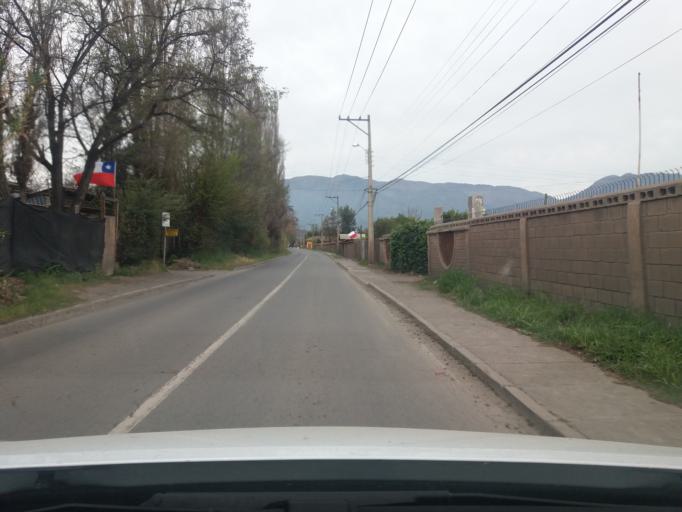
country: CL
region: Valparaiso
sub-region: Provincia de Los Andes
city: Los Andes
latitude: -32.8469
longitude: -70.6284
